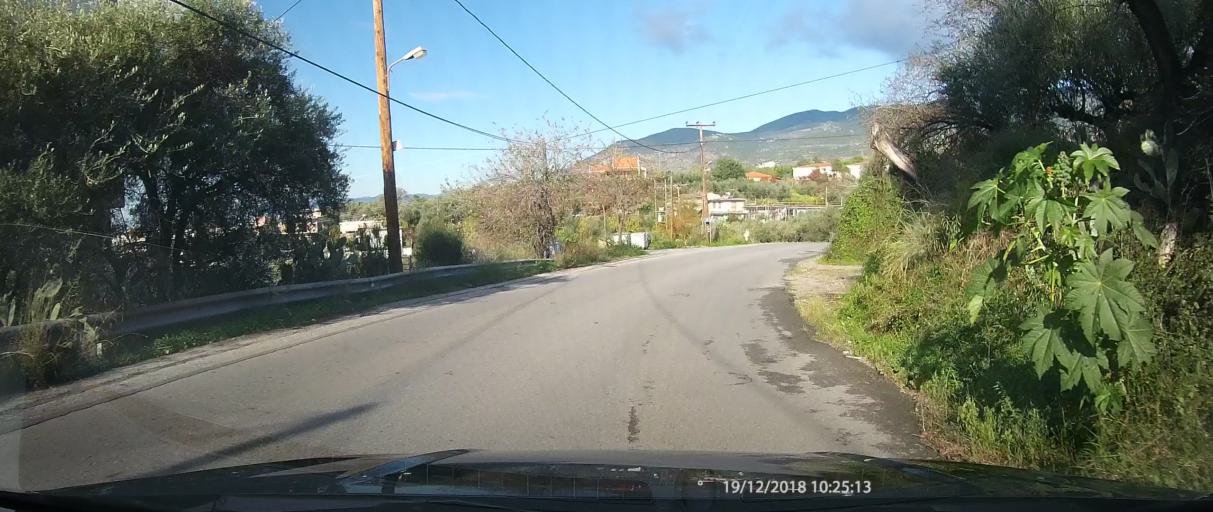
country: GR
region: Peloponnese
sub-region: Nomos Messinias
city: Kalamata
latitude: 37.0467
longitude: 22.1332
